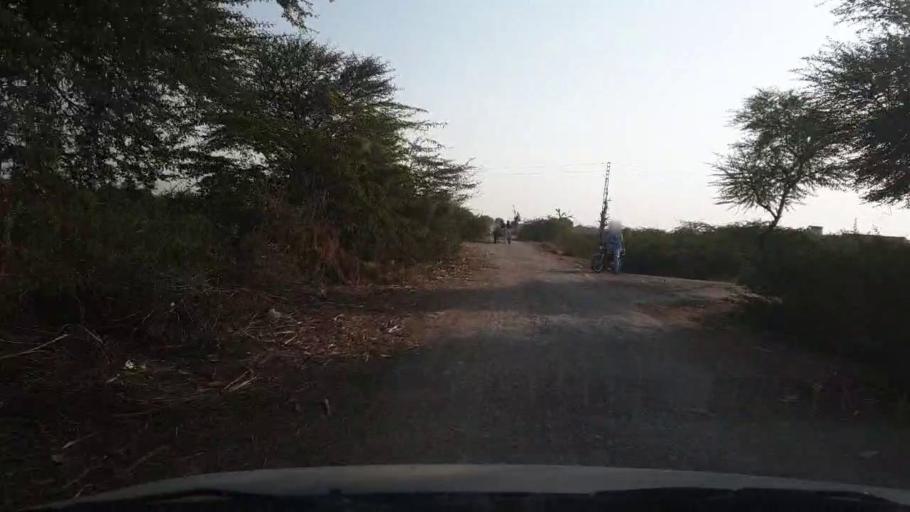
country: PK
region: Sindh
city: Samaro
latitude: 25.2633
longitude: 69.3587
